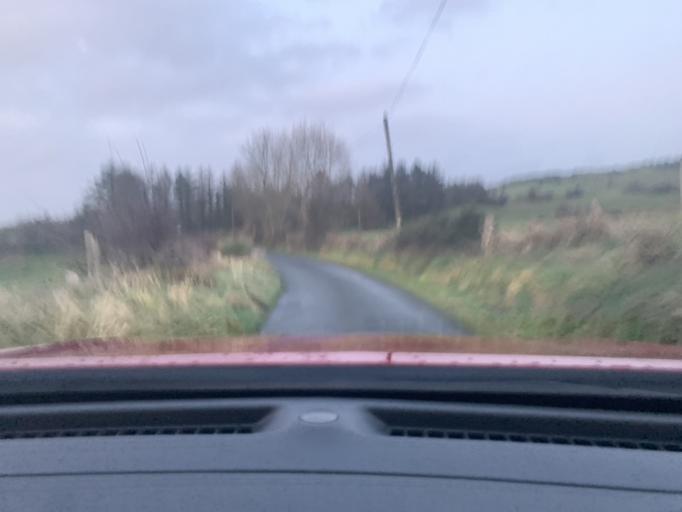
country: IE
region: Connaught
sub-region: Sligo
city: Ballymote
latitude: 54.0717
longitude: -8.3927
